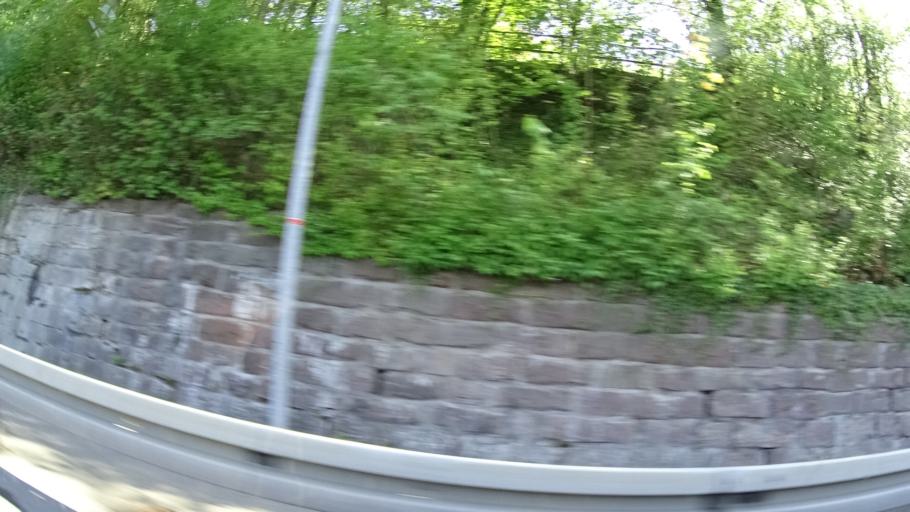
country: DE
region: Baden-Wuerttemberg
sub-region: Karlsruhe Region
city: Rohrdorf
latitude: 48.5684
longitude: 8.6980
